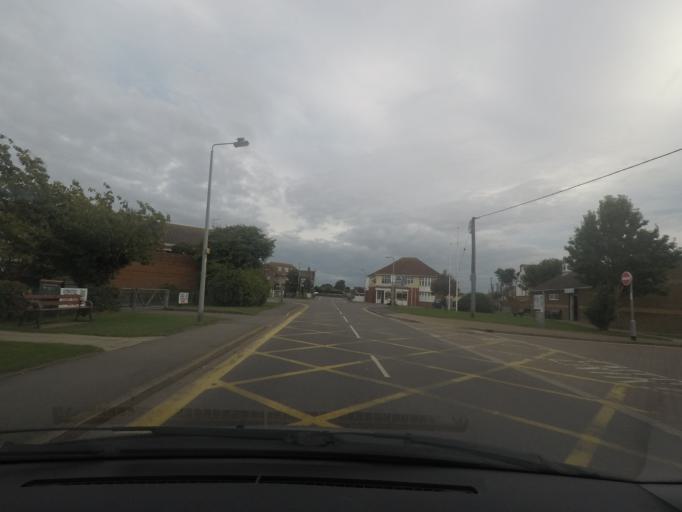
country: GB
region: England
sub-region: Lincolnshire
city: Chapel Saint Leonards
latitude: 53.2244
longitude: 0.3365
